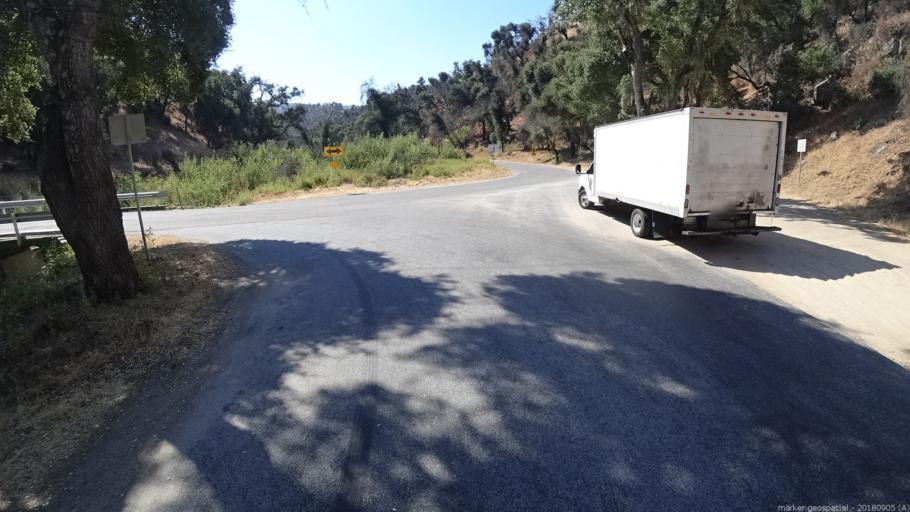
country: US
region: California
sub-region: Monterey County
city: Gonzales
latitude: 36.3911
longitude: -121.5952
